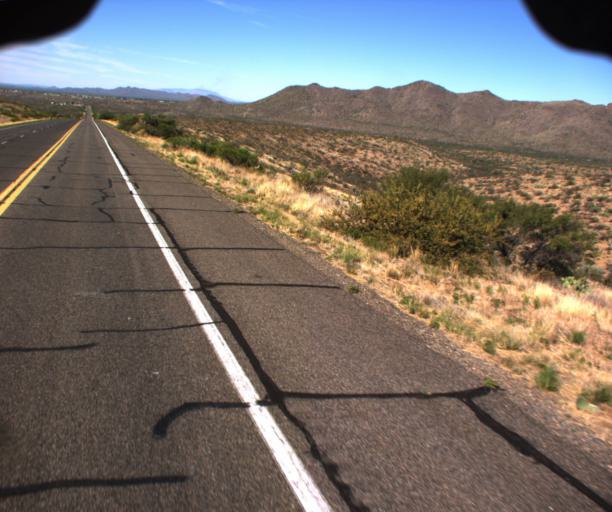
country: US
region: Arizona
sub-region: Yavapai County
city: Congress
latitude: 34.1998
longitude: -112.8085
